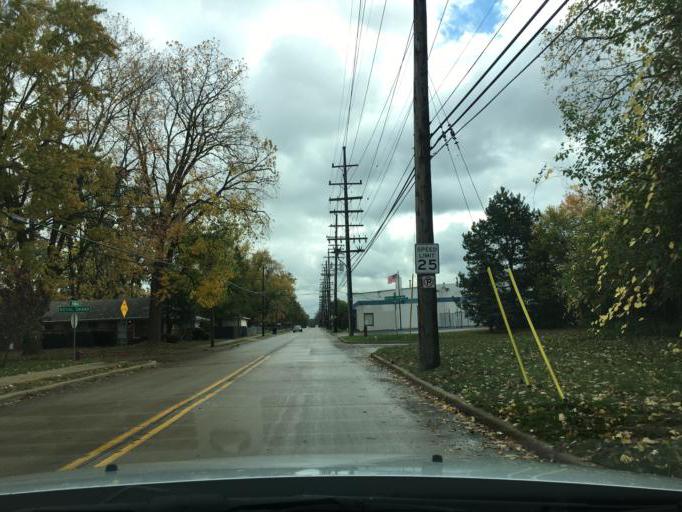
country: US
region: Michigan
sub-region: Wayne County
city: Redford
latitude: 42.3805
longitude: -83.2945
